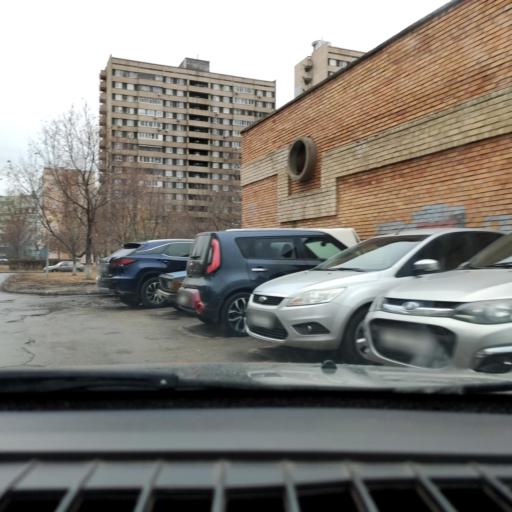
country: RU
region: Samara
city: Tol'yatti
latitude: 53.5418
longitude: 49.3212
